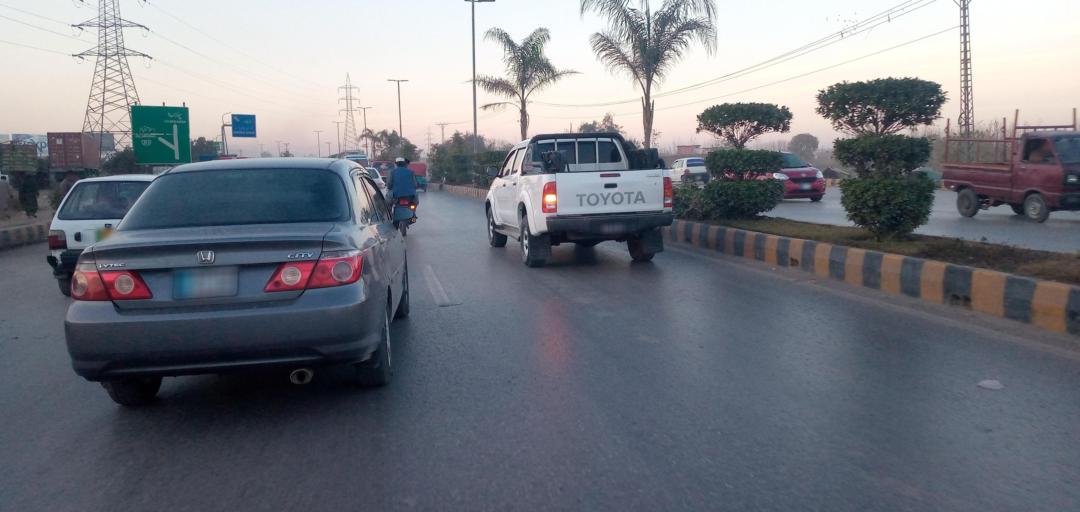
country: PK
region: Khyber Pakhtunkhwa
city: Peshawar
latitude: 34.0246
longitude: 71.6199
